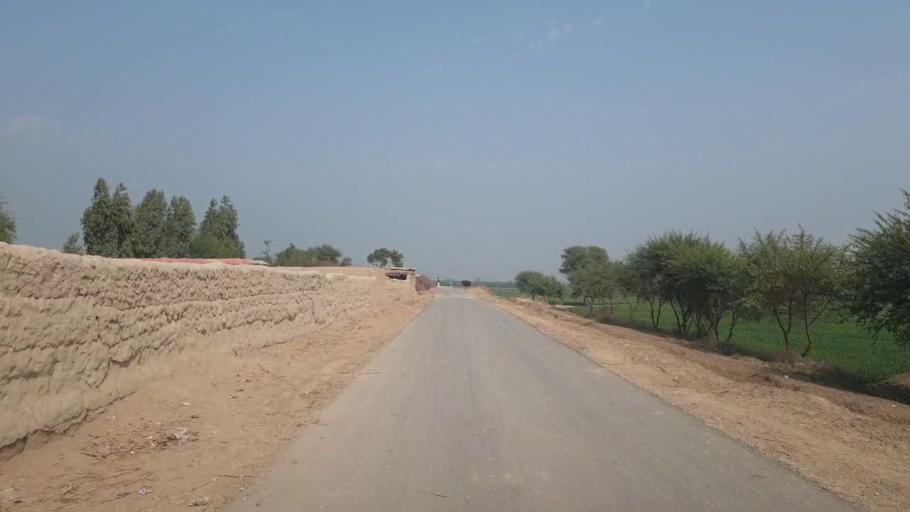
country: PK
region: Sindh
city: Hala
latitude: 25.7804
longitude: 68.3987
